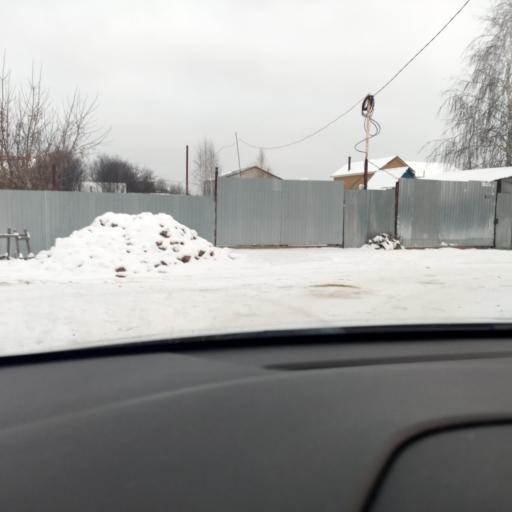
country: RU
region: Tatarstan
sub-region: Gorod Kazan'
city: Kazan
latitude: 55.8700
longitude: 49.1440
